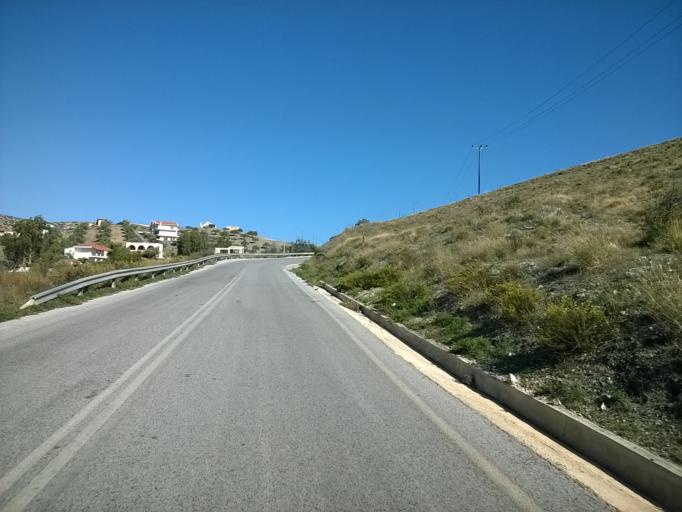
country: GR
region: Attica
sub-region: Nomarchia Anatolikis Attikis
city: Keratea
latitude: 37.7724
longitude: 23.9894
